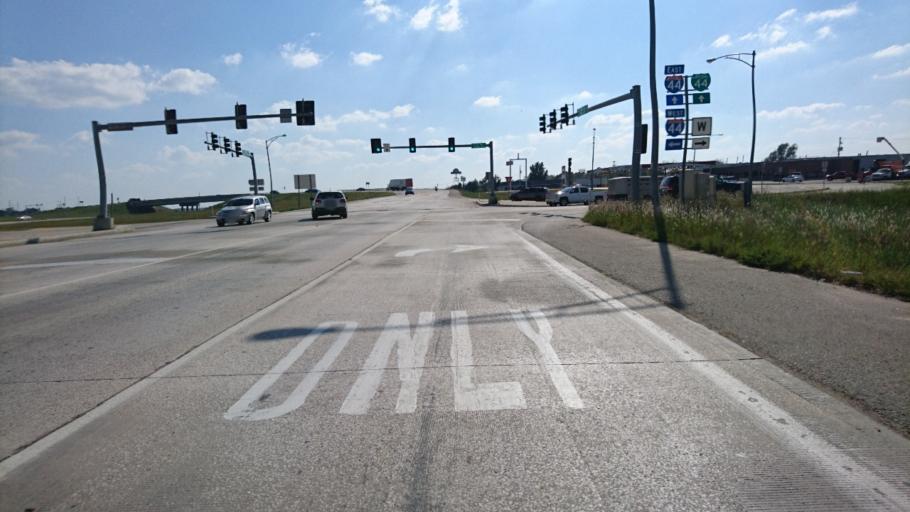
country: US
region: Missouri
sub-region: Laclede County
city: Lebanon
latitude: 37.6502
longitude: -92.6682
